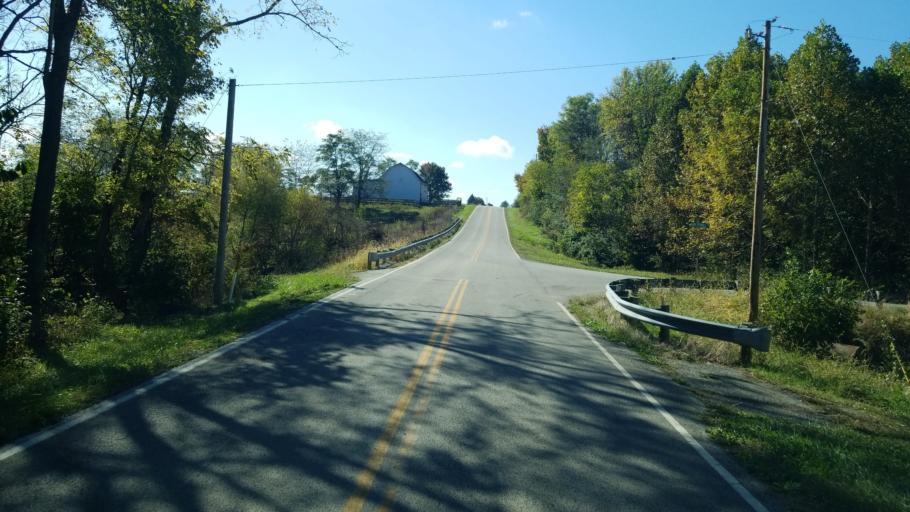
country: US
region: Ohio
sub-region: Highland County
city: Leesburg
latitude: 39.2981
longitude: -83.5794
